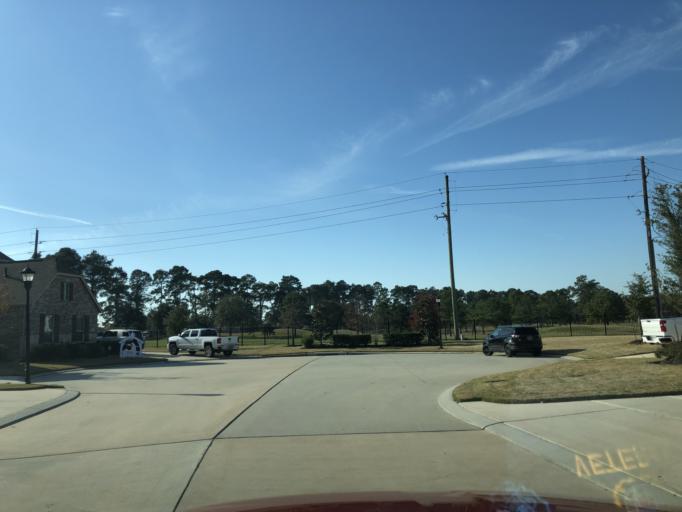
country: US
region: Texas
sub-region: Harris County
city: Tomball
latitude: 30.0318
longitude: -95.5582
